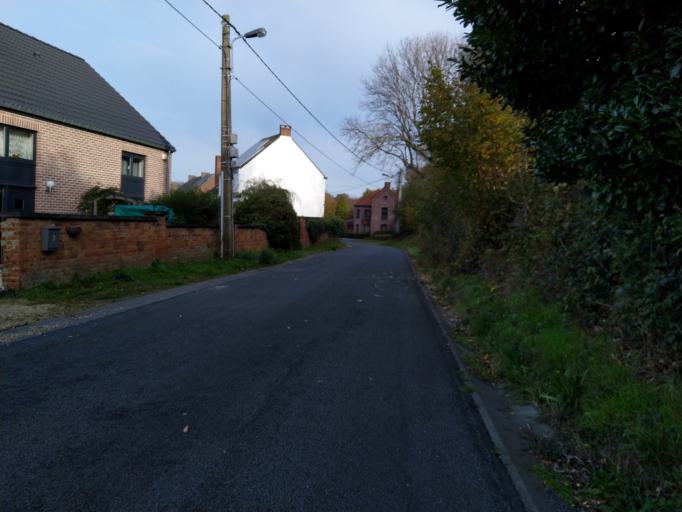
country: BE
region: Wallonia
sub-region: Province du Hainaut
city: Saint-Ghislain
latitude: 50.5078
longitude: 3.7964
